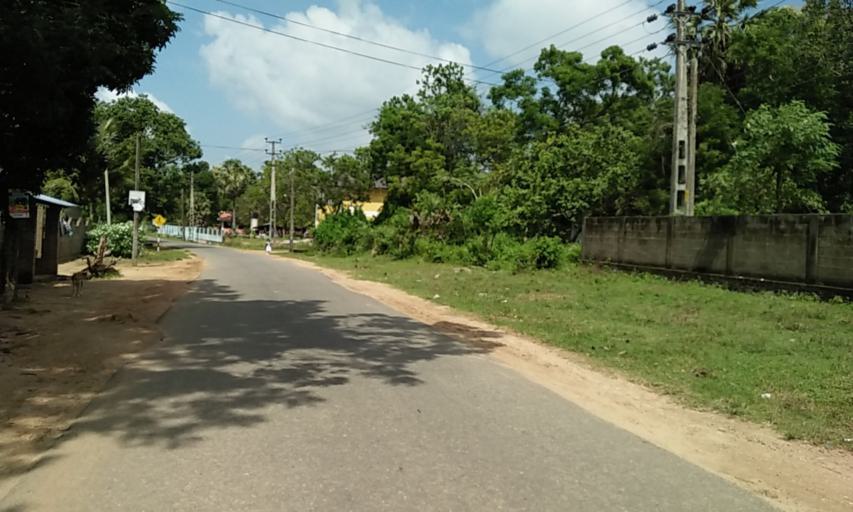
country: LK
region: Eastern Province
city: Ampara
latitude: 7.3361
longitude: 81.7431
